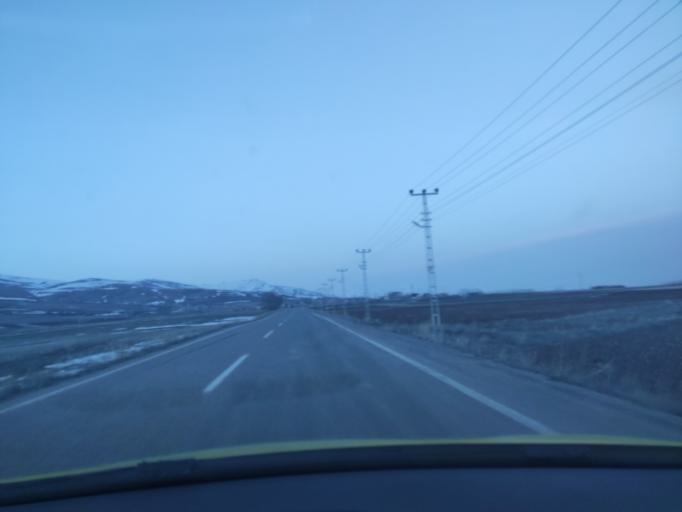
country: TR
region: Bayburt
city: Aydintepe
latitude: 40.3778
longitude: 40.1185
